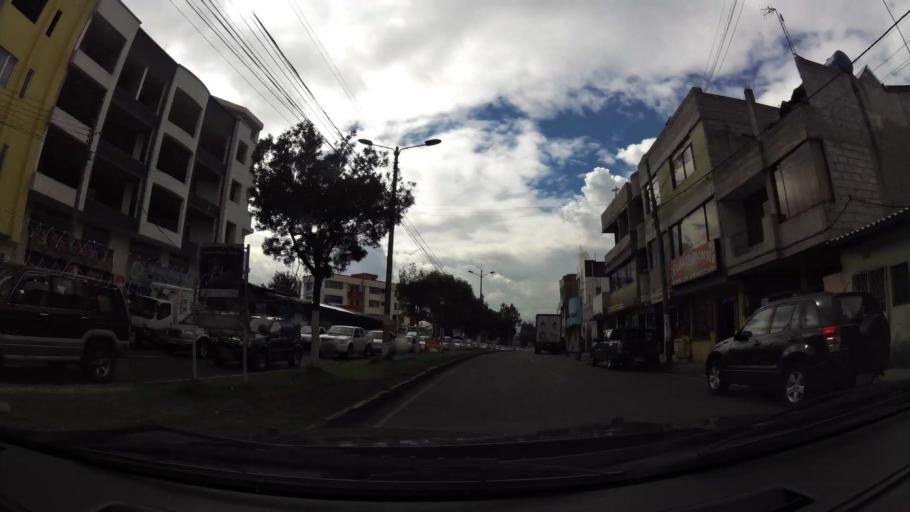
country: EC
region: Pichincha
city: Sangolqui
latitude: -0.3238
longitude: -78.4498
